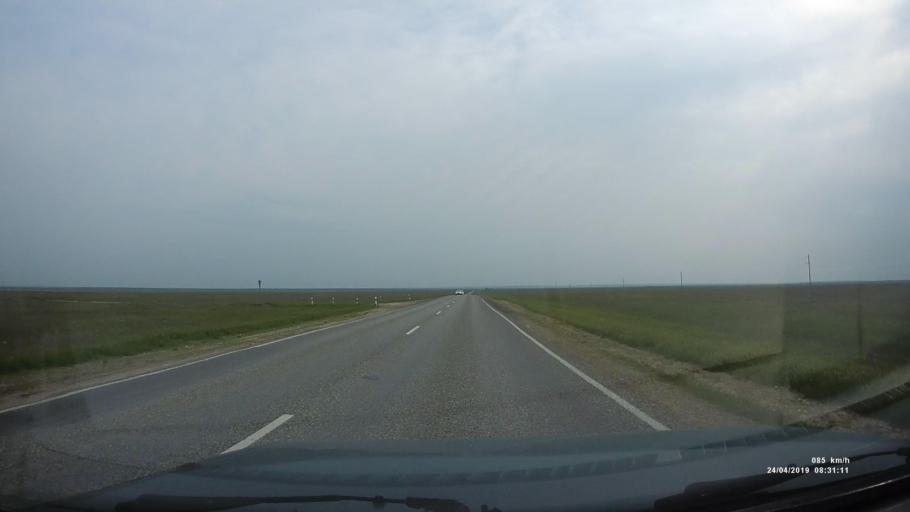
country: RU
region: Kalmykiya
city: Priyutnoye
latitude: 46.1652
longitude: 43.8565
